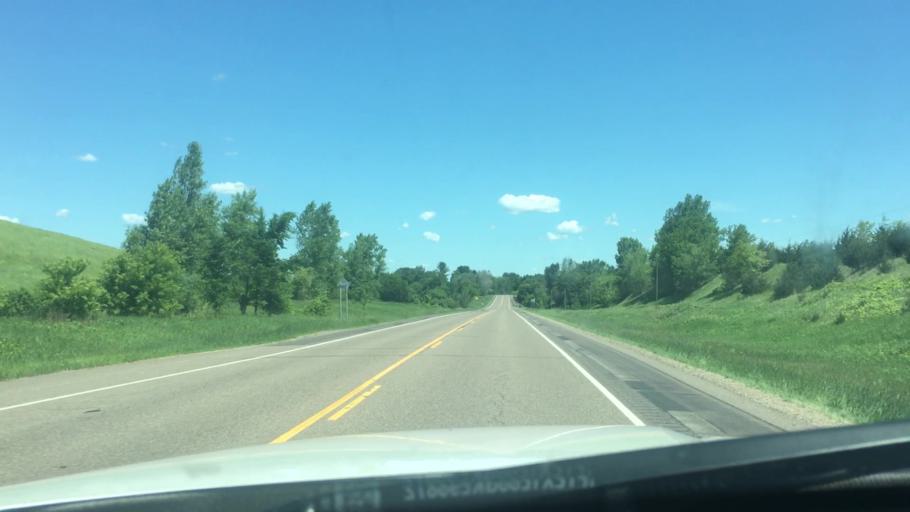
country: US
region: Wisconsin
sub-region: Polk County
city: Osceola
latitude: 45.3519
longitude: -92.7128
